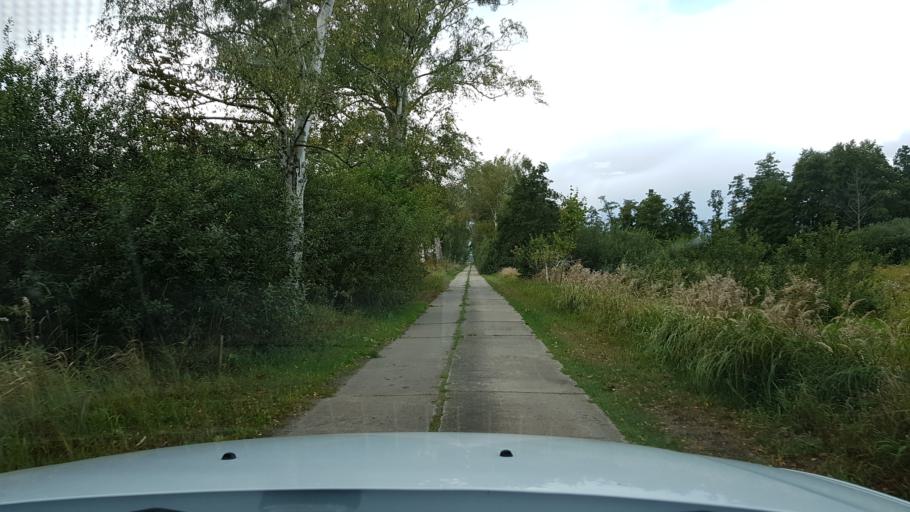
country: PL
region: West Pomeranian Voivodeship
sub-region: Powiat policki
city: Przeclaw
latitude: 53.3205
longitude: 14.5257
